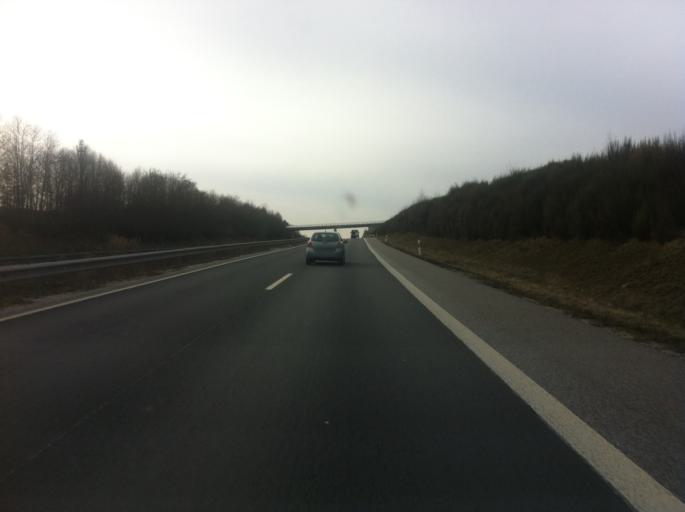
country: DE
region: Rheinland-Pfalz
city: Niedersohren
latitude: 49.9371
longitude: 7.3252
